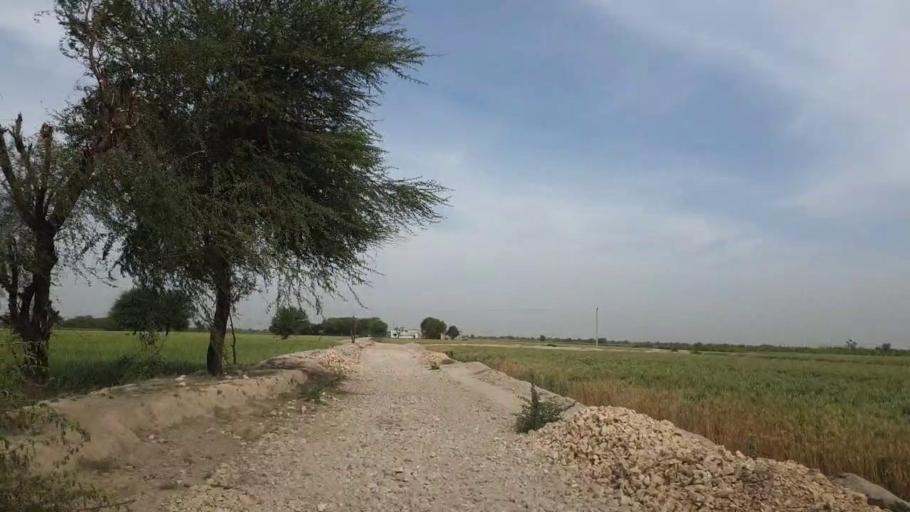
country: PK
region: Sindh
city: Kunri
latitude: 25.1820
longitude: 69.5887
